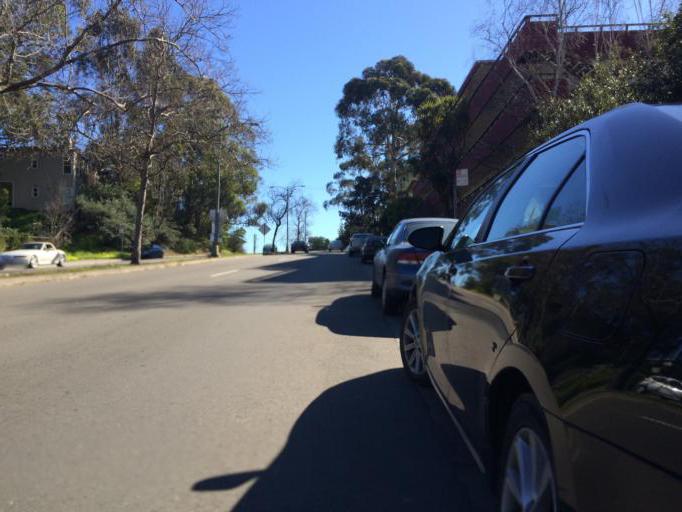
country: US
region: California
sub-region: Alameda County
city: Piedmont
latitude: 37.8331
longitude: -122.2503
